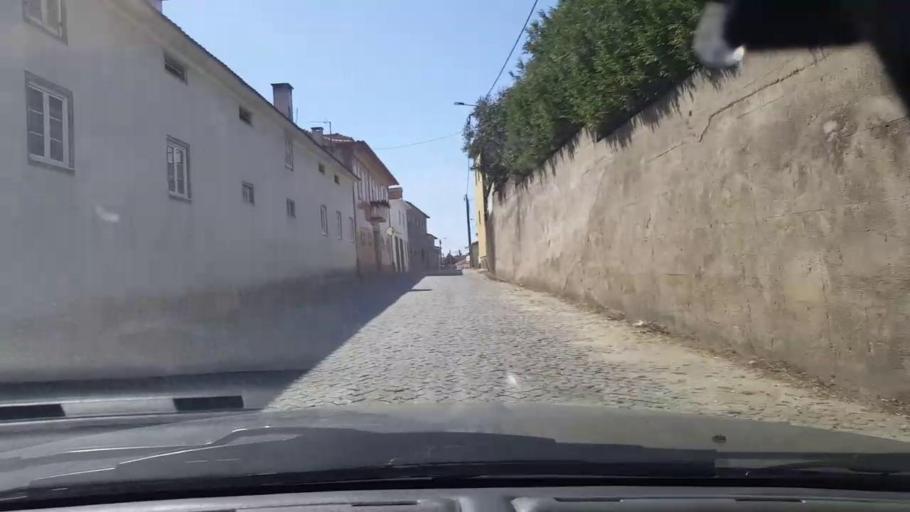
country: PT
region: Porto
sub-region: Matosinhos
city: Lavra
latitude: 41.2801
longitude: -8.7027
